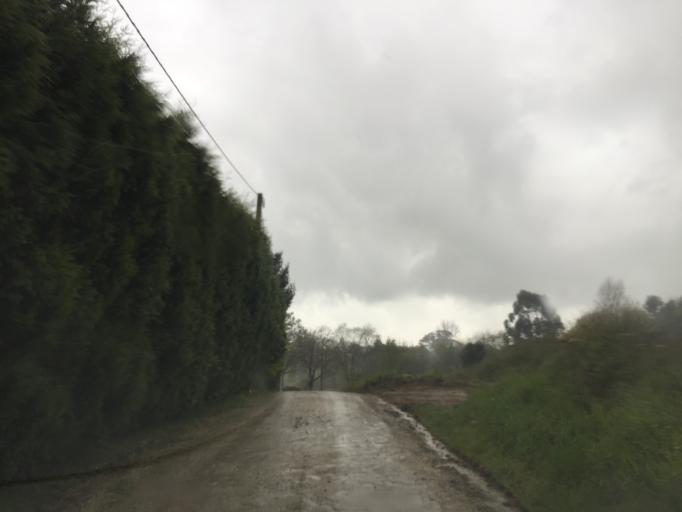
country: ES
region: Asturias
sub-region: Province of Asturias
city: Arriba
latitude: 43.5278
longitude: -5.5857
